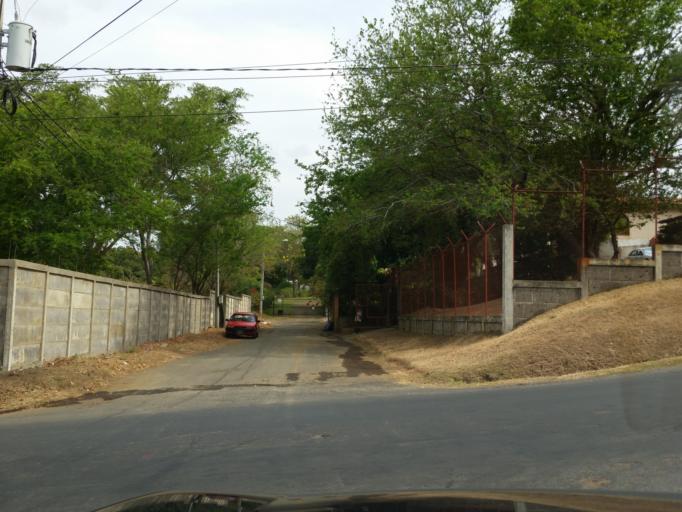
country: NI
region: Managua
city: Managua
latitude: 12.0910
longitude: -86.2434
